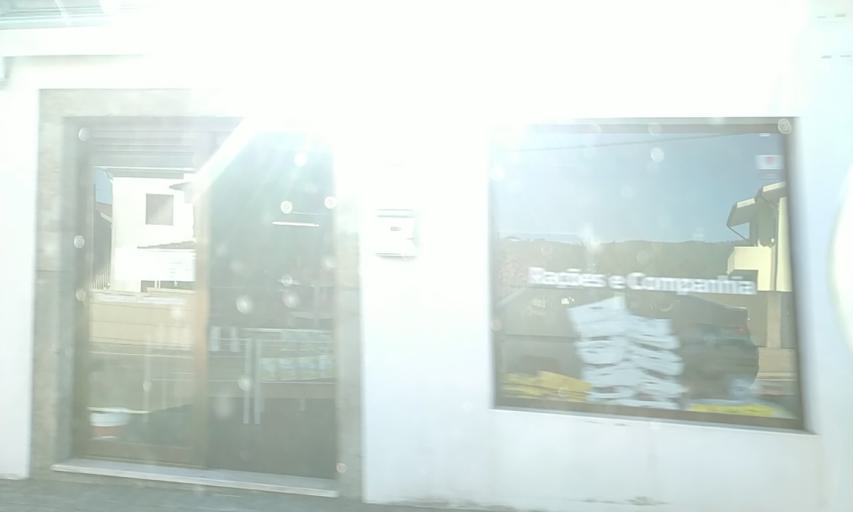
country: PT
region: Porto
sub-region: Santo Tirso
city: Sao Miguel do Couto
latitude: 41.2879
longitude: -8.4717
